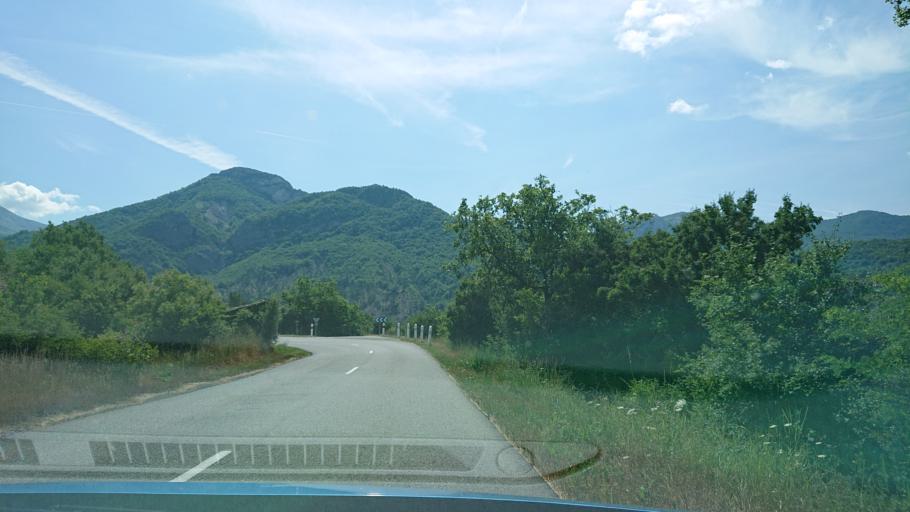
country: FR
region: Provence-Alpes-Cote d'Azur
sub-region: Departement des Alpes-de-Haute-Provence
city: Sisteron
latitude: 44.2822
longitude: 6.0160
